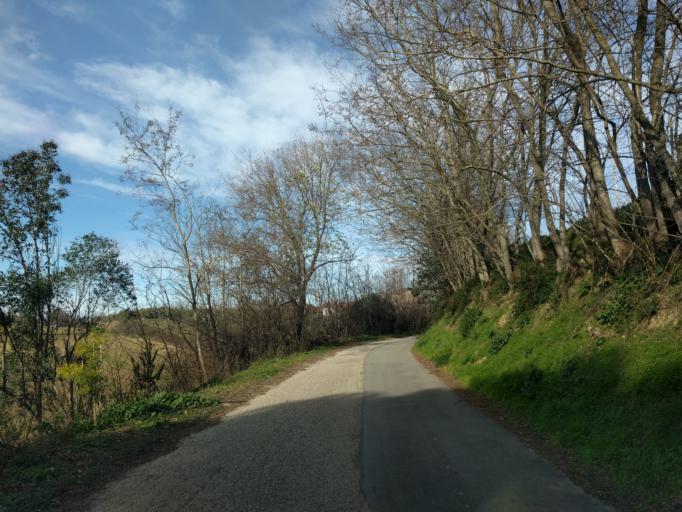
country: IT
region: The Marches
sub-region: Provincia di Pesaro e Urbino
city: Cuccurano
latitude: 43.8088
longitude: 12.9518
